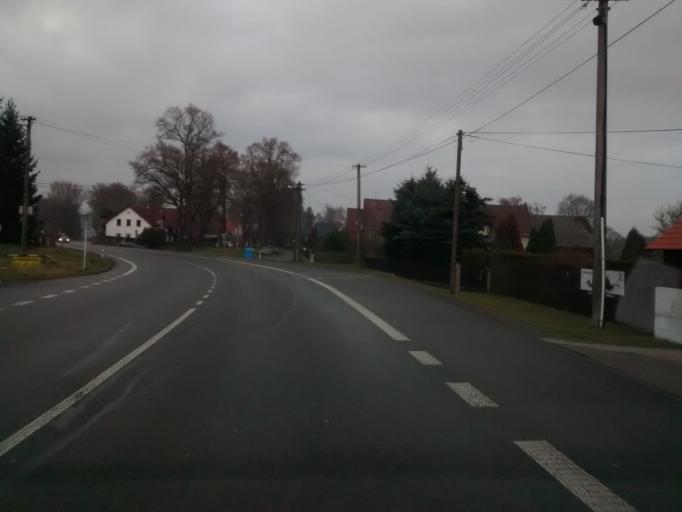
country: CZ
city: Doksy
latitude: 50.5471
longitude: 14.6703
